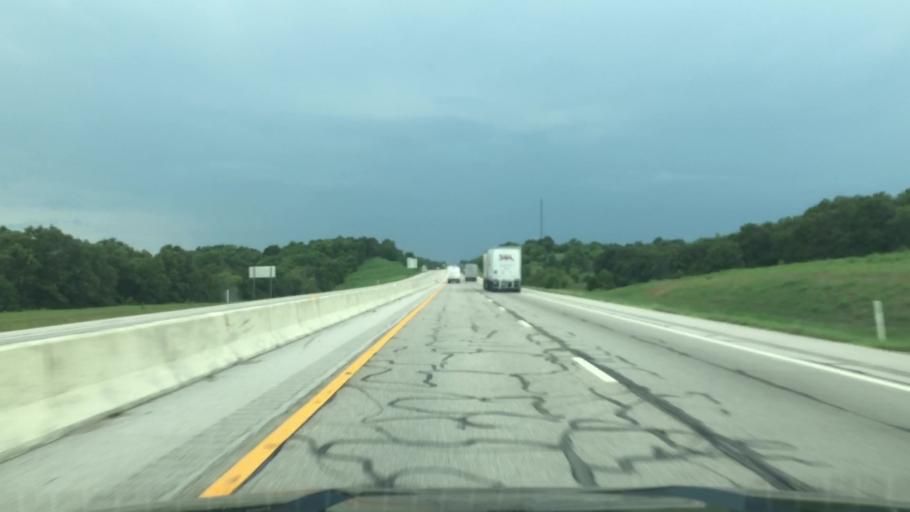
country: US
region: Oklahoma
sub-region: Rogers County
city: Bushyhead
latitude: 36.4286
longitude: -95.3901
